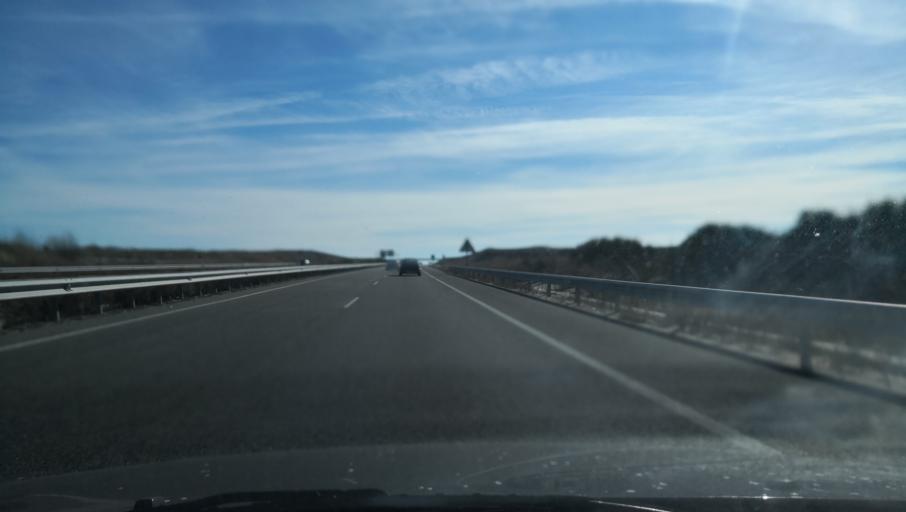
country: ES
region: Castille and Leon
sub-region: Provincia de Salamanca
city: Penaranda de Bracamonte
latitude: 40.9139
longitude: -5.1913
